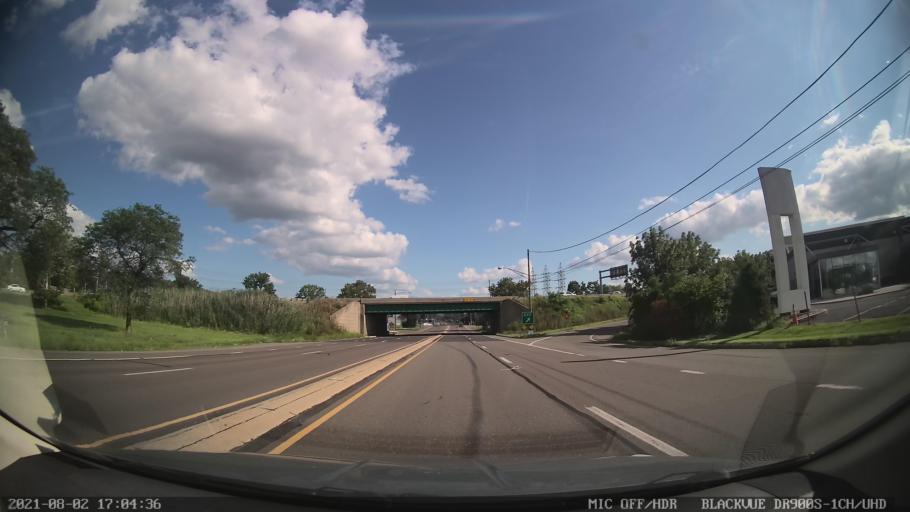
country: US
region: Pennsylvania
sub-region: Berks County
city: Hyde Park
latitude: 40.3703
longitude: -75.9330
